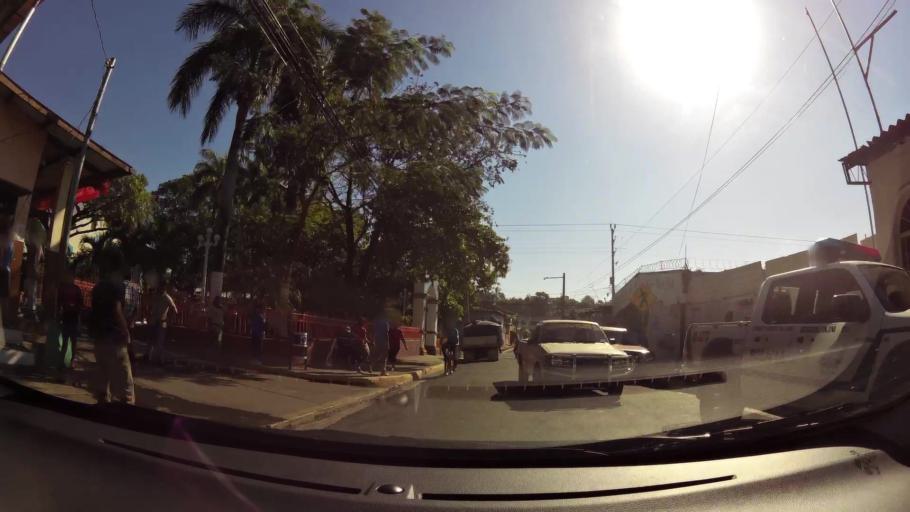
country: SV
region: Sonsonate
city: Sonzacate
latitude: 13.7356
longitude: -89.7160
